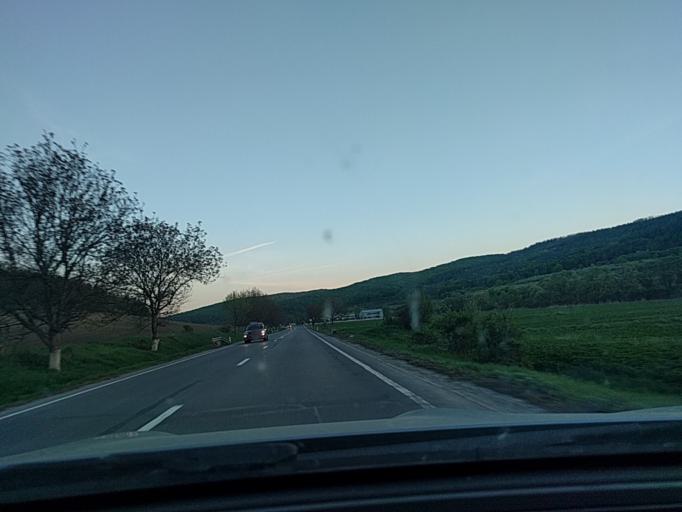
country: RO
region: Mures
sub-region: Comuna Nades
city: Nades
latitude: 46.3367
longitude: 24.7107
